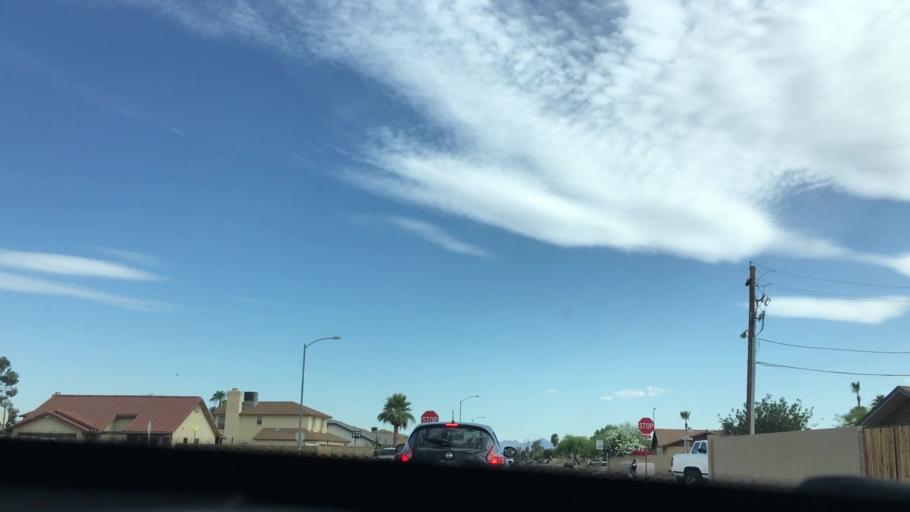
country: US
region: Arizona
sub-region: Maricopa County
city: Peoria
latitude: 33.5890
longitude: -112.2289
